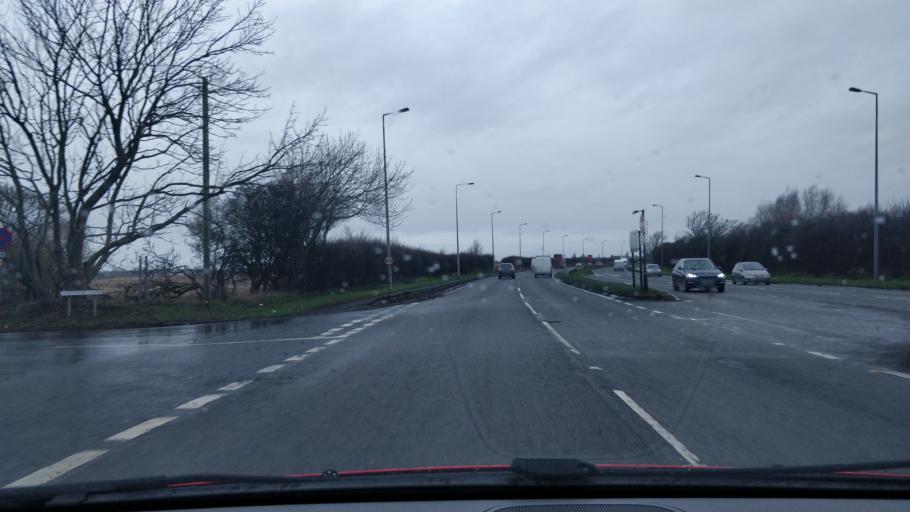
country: GB
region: England
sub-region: Sefton
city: Hightown
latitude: 53.5364
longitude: -3.0451
